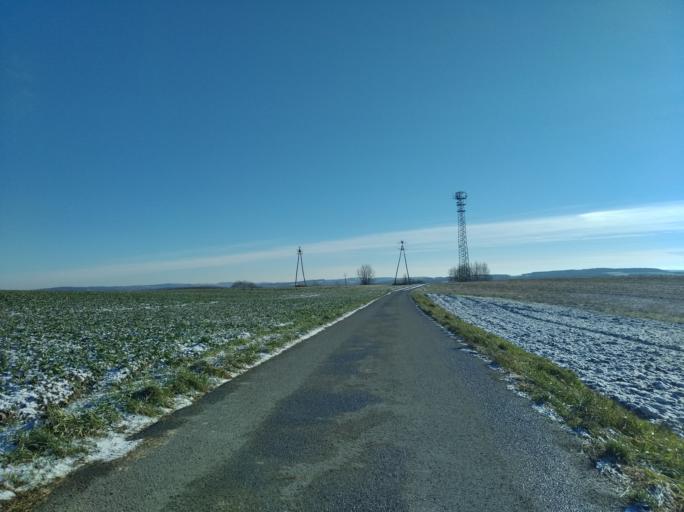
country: PL
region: Subcarpathian Voivodeship
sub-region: Powiat ropczycko-sedziszowski
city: Iwierzyce
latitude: 49.9510
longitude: 21.7609
